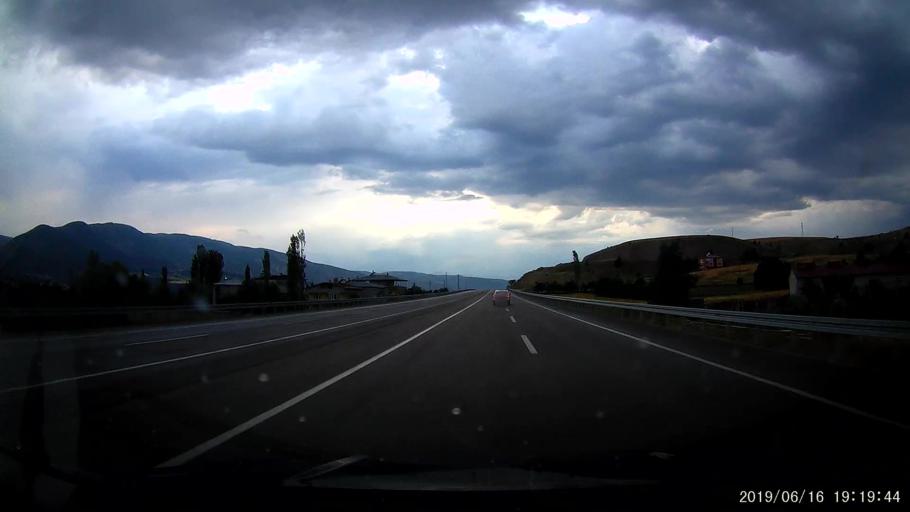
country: TR
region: Sivas
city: Akincilar
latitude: 40.0948
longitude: 38.4202
